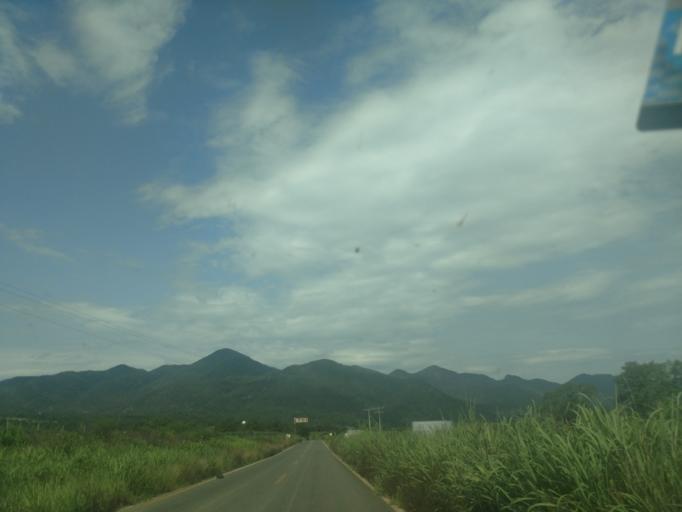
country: MX
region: Jalisco
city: Mascota
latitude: 20.4444
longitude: -104.7569
